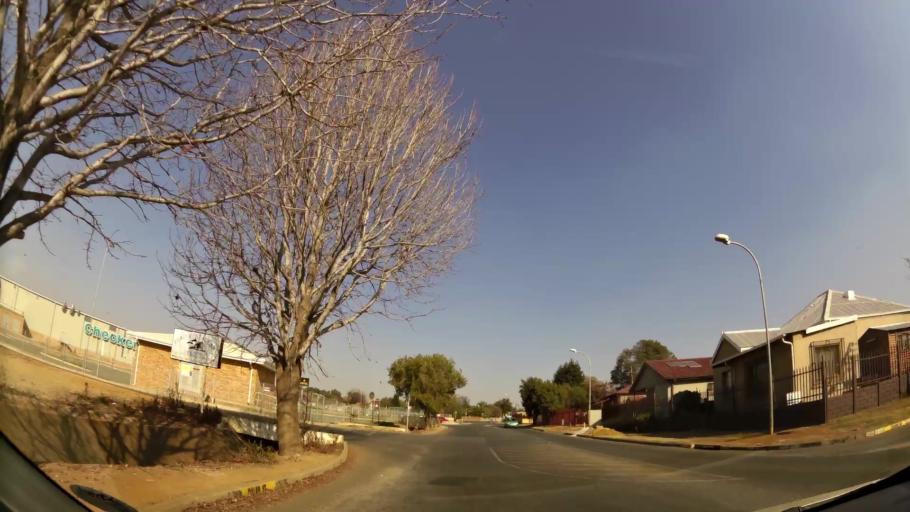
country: ZA
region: Gauteng
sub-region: West Rand District Municipality
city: Randfontein
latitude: -26.1713
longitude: 27.6894
